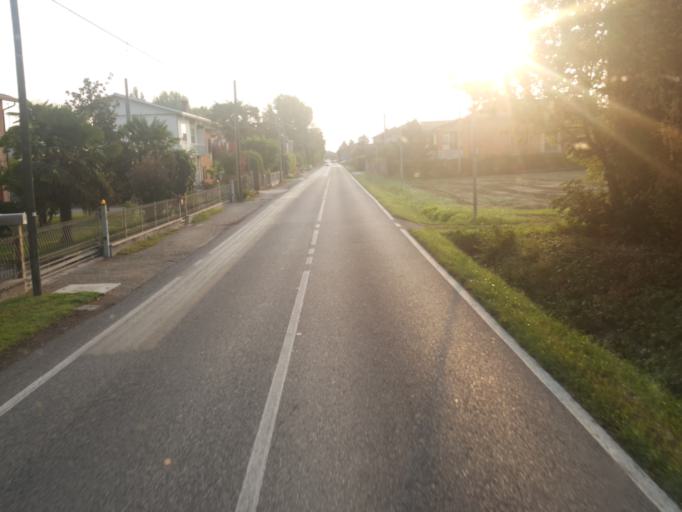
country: IT
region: Emilia-Romagna
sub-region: Provincia di Ravenna
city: Lavezzola
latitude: 44.5580
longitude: 11.8707
